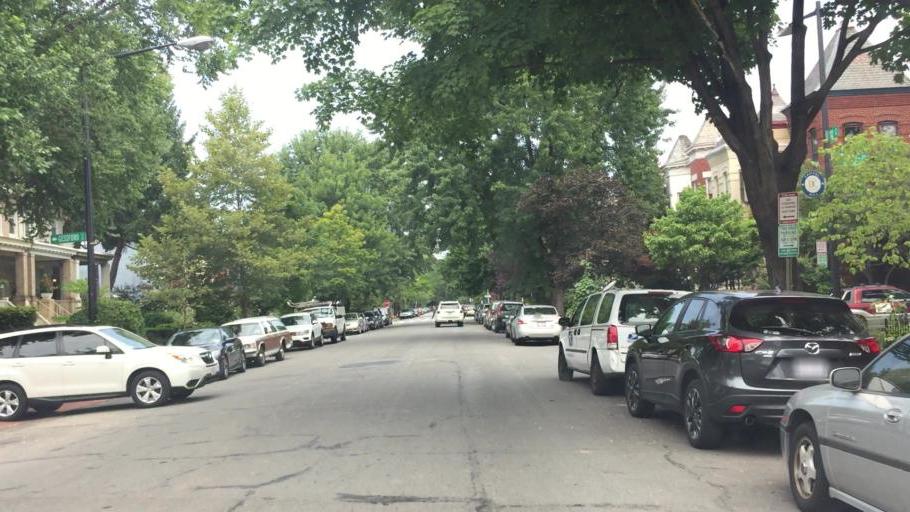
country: US
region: Washington, D.C.
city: Washington, D.C.
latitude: 38.8866
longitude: -76.9902
